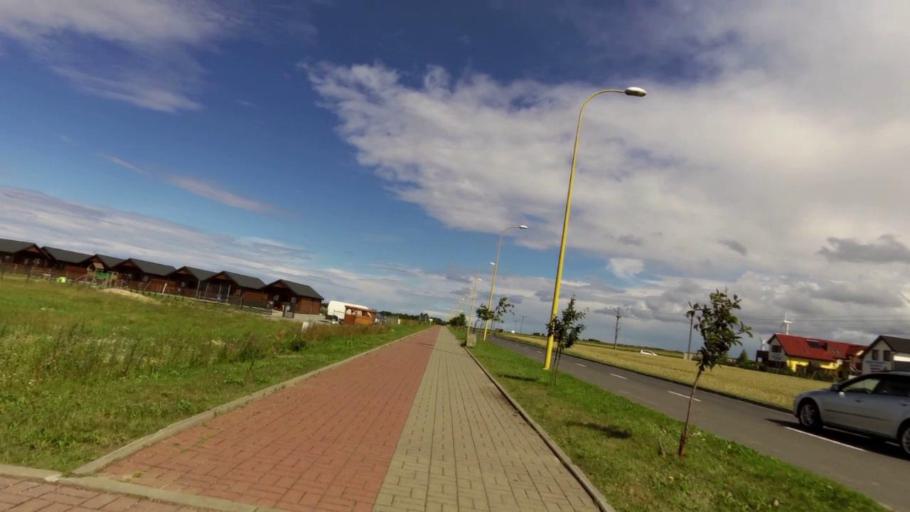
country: PL
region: West Pomeranian Voivodeship
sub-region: Powiat slawienski
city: Darlowo
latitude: 54.4368
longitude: 16.4094
